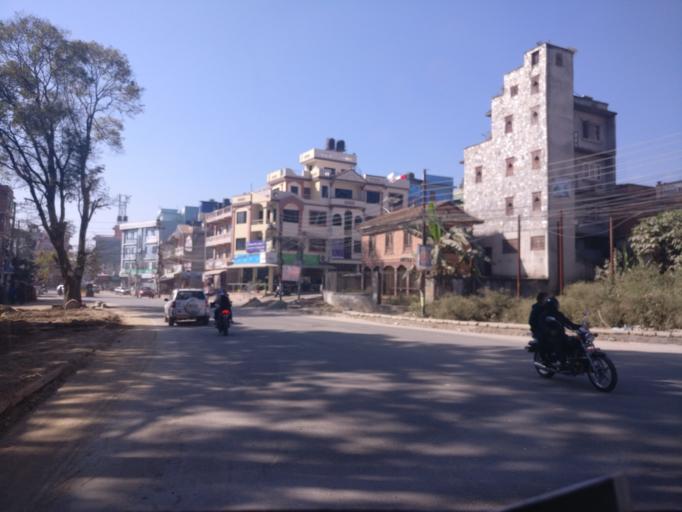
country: NP
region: Central Region
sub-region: Bagmati Zone
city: Patan
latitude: 27.6537
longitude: 85.3051
